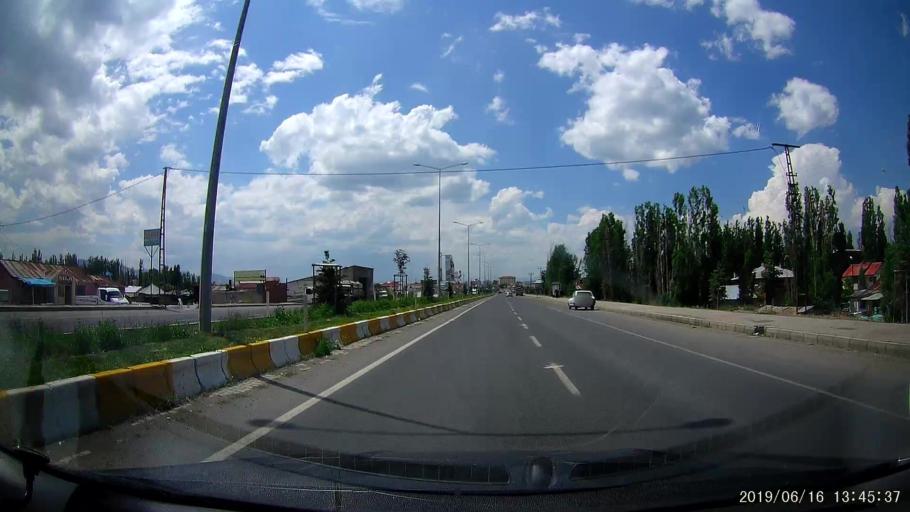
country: TR
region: Agri
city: Agri
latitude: 39.7095
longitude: 43.0431
